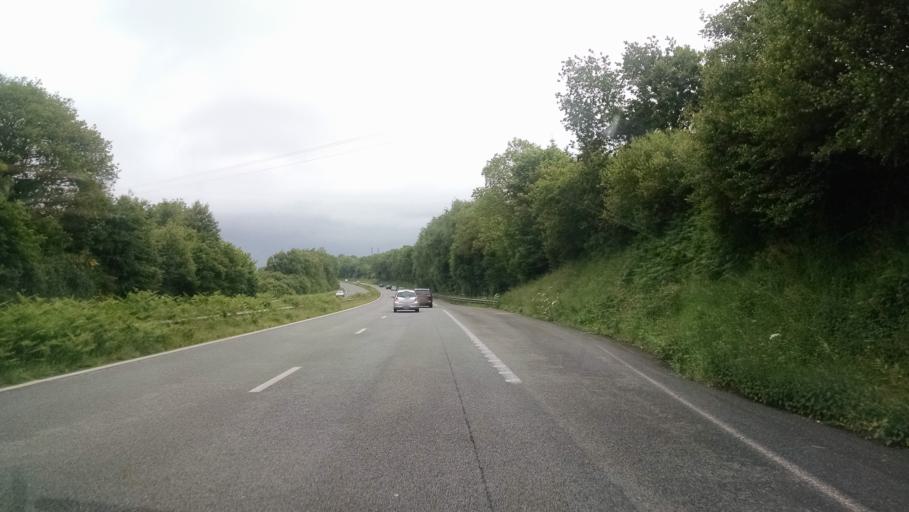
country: FR
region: Brittany
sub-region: Departement du Finistere
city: Melgven
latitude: 47.9124
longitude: -3.8690
